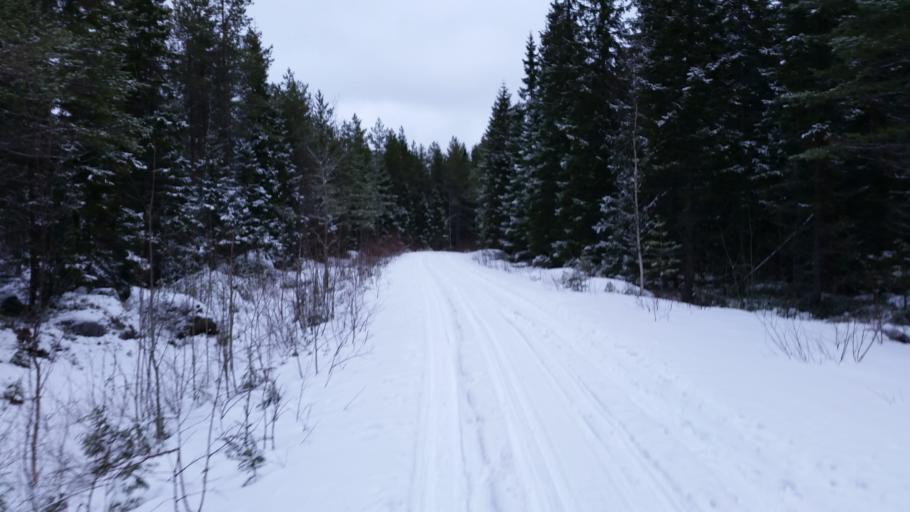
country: SE
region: Vaesterbotten
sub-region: Umea Kommun
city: Saevar
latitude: 63.9168
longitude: 20.7697
